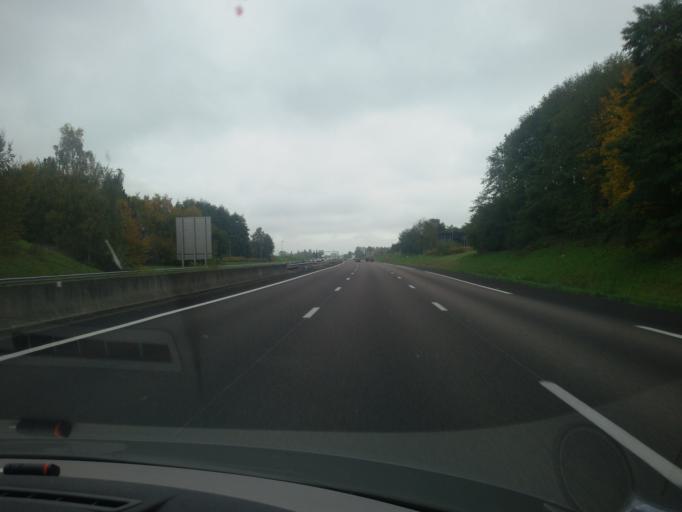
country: FR
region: Haute-Normandie
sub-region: Departement de l'Eure
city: Corneville-sur-Risle
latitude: 49.3778
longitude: 0.6231
